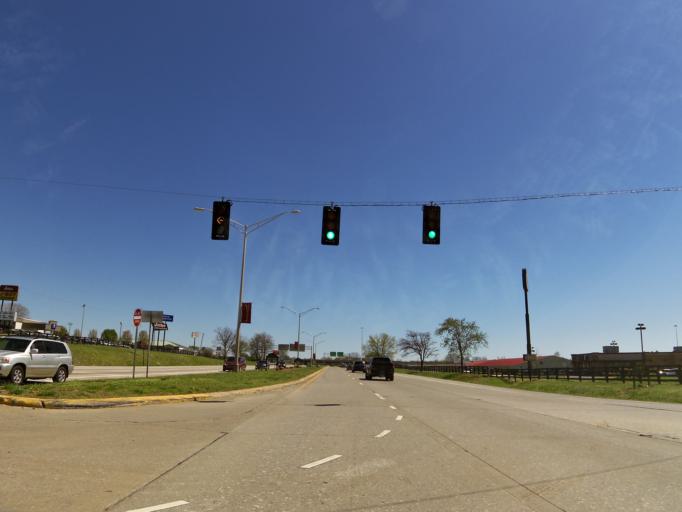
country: US
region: Kentucky
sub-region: Warren County
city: Bowling Green
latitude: 37.0079
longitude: -86.3744
